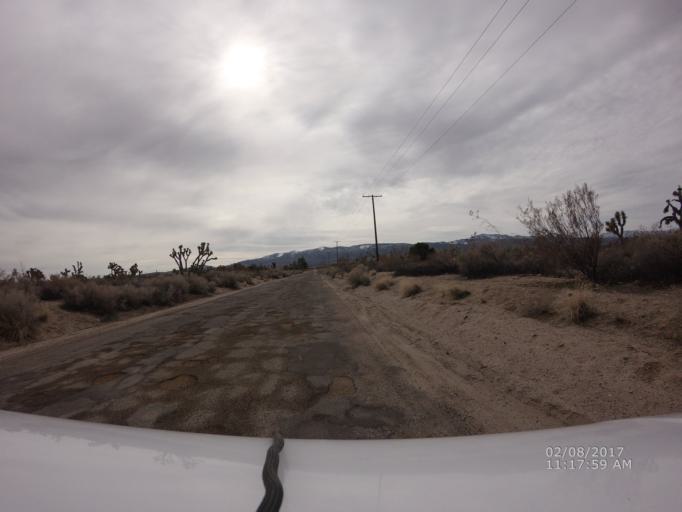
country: US
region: California
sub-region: San Bernardino County
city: Pinon Hills
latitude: 34.4941
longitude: -117.6600
